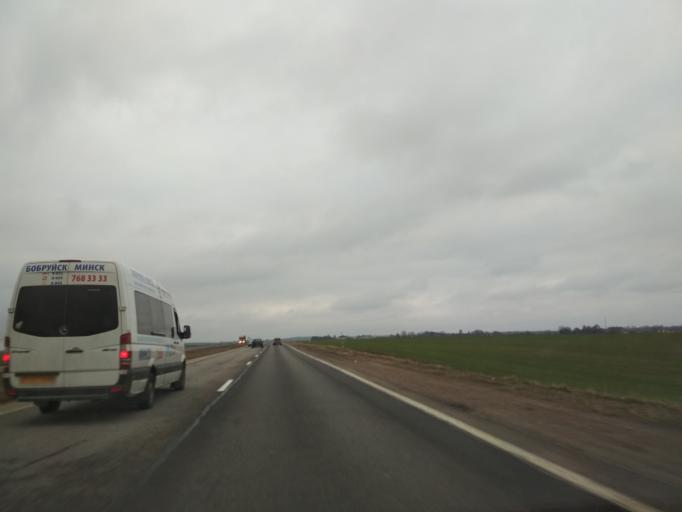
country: BY
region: Minsk
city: Blon'
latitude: 53.5828
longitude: 28.1165
